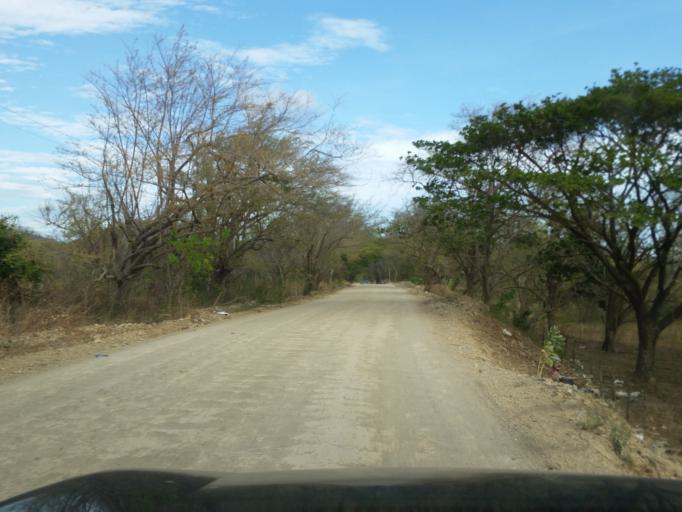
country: NI
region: Rivas
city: Tola
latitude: 11.4263
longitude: -86.0134
